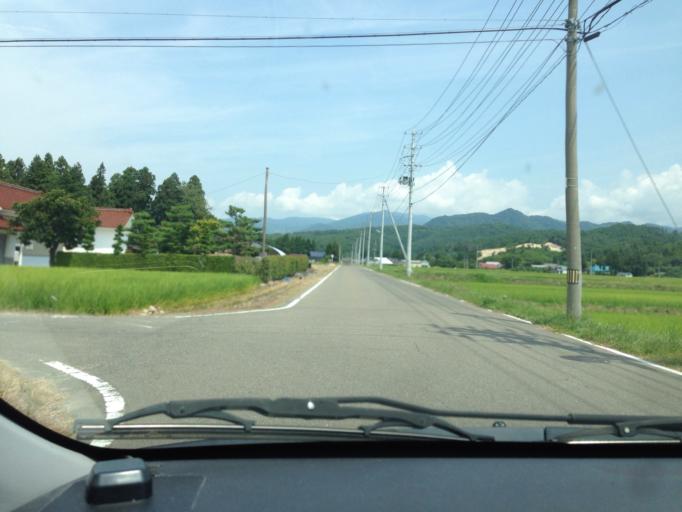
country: JP
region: Fukushima
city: Kitakata
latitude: 37.6865
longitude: 139.8829
